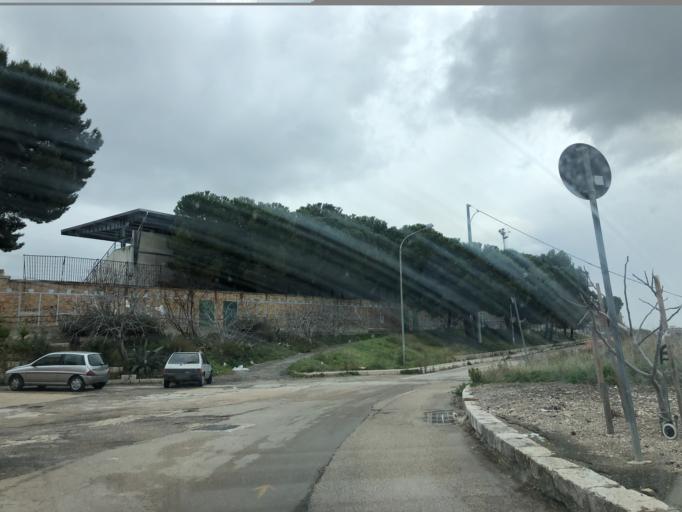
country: IT
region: Apulia
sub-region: Provincia di Foggia
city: Lucera
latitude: 41.5062
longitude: 15.3267
